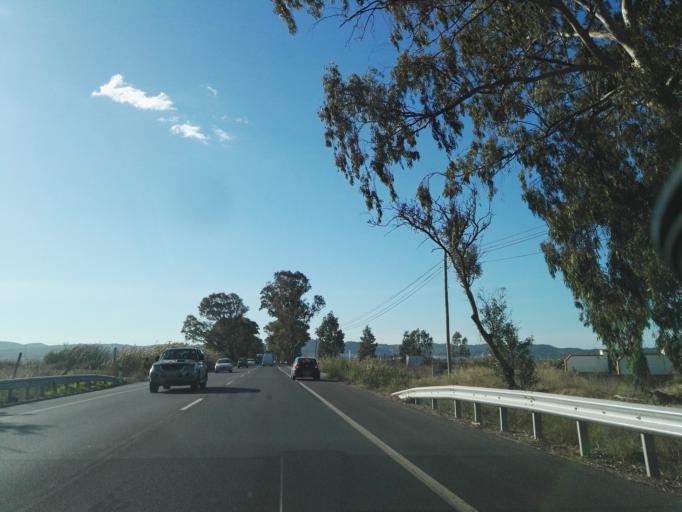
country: PT
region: Lisbon
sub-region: Vila Franca de Xira
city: Vila Franca de Xira
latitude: 38.9384
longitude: -8.9334
